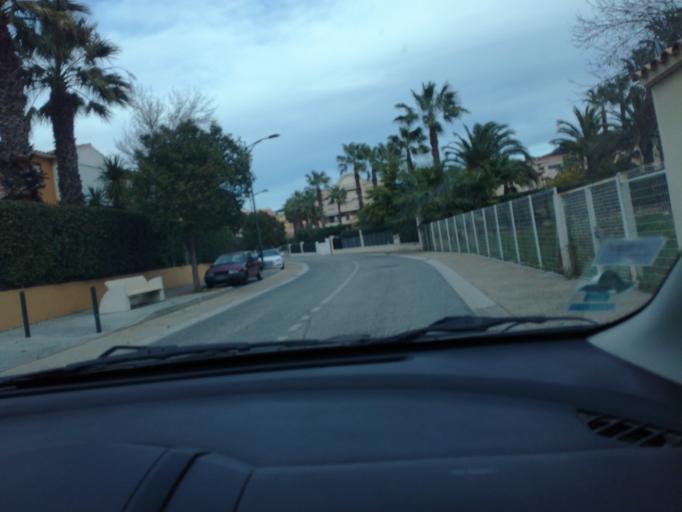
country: FR
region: Provence-Alpes-Cote d'Azur
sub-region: Departement du Var
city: Hyeres
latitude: 43.1202
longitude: 6.1165
